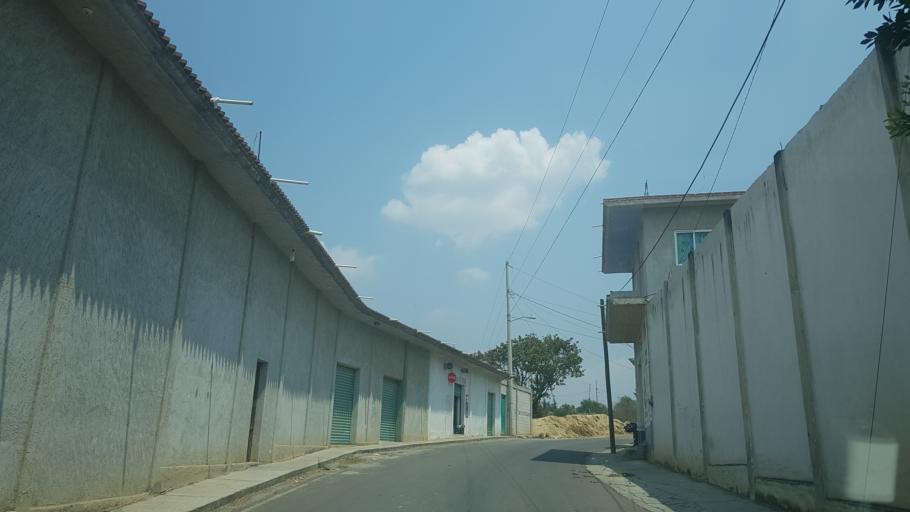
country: MX
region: Puebla
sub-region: San Nicolas de los Ranchos
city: San Pedro Yancuitlalpan
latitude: 19.0801
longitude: -98.4806
